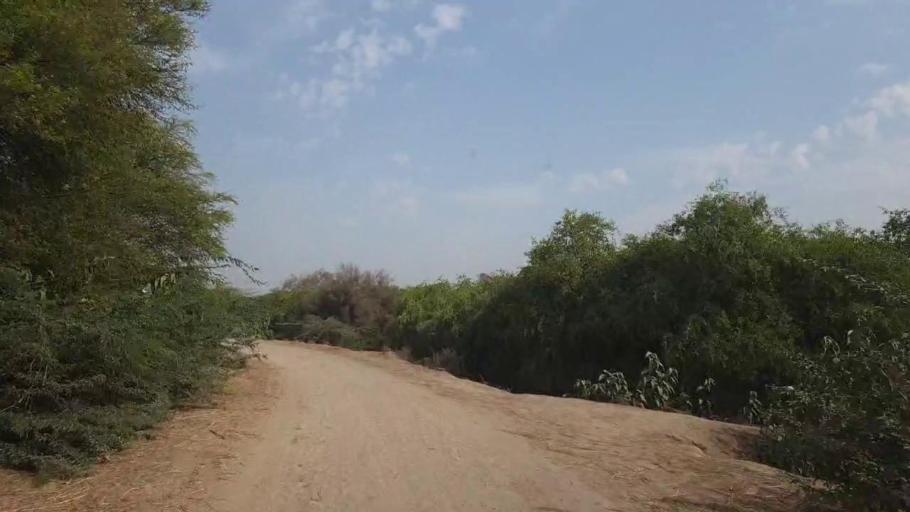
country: PK
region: Sindh
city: Rajo Khanani
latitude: 24.9609
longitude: 68.9863
